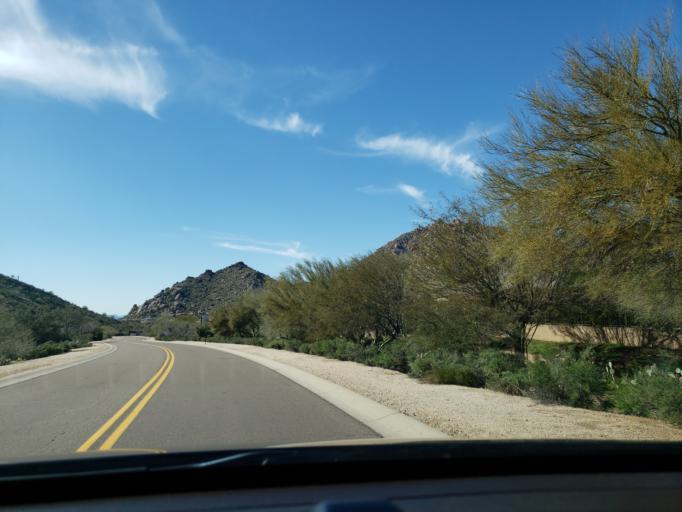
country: US
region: Arizona
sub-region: Maricopa County
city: Fountain Hills
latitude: 33.7052
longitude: -111.8274
